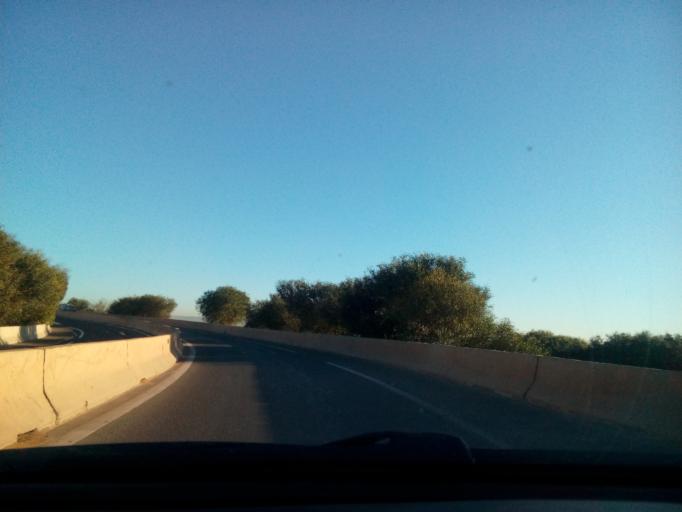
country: DZ
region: Relizane
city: Djidiouia
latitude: 35.8875
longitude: 0.7016
